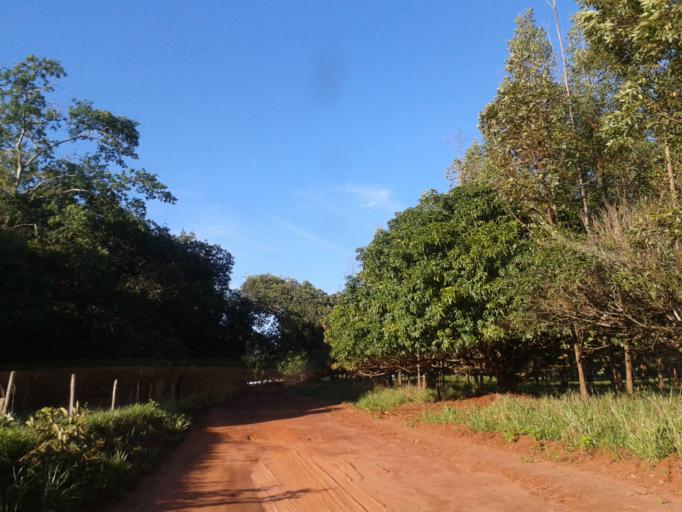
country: BR
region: Minas Gerais
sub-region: Santa Vitoria
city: Santa Vitoria
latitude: -18.9702
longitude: -49.8837
